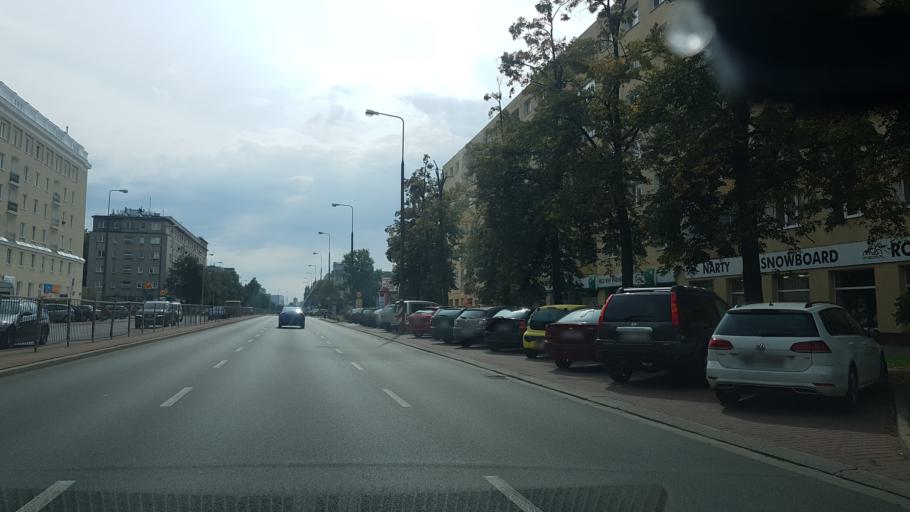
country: PL
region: Masovian Voivodeship
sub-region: Warszawa
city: Mokotow
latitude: 52.1991
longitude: 21.0120
